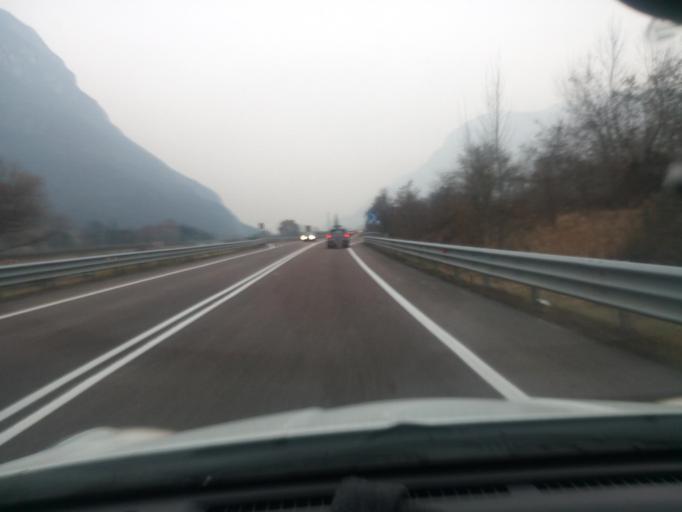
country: IT
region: Trentino-Alto Adige
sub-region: Provincia di Trento
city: Mattarello
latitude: 45.9944
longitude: 11.1210
